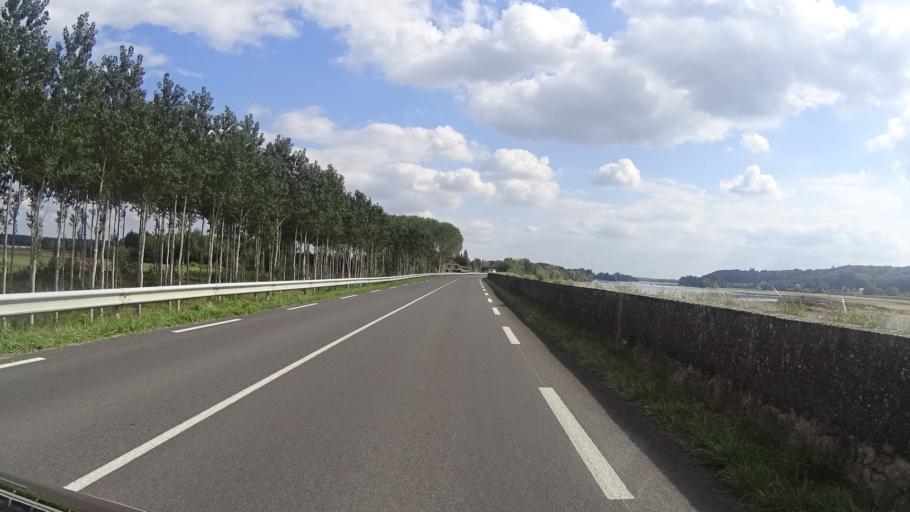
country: FR
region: Pays de la Loire
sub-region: Departement de Maine-et-Loire
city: Chenehutte-Treves-Cunault
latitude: 47.3236
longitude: -0.1674
